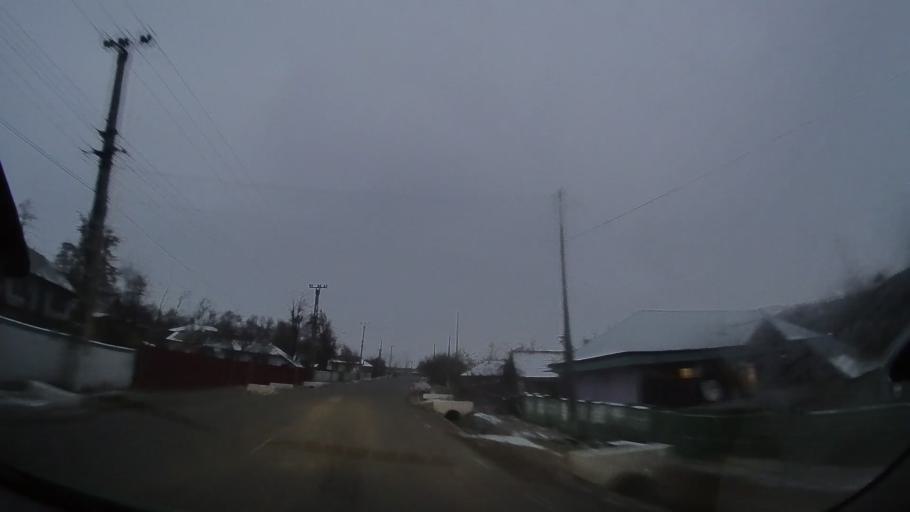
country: RO
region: Vaslui
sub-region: Comuna Vutcani
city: Vutcani
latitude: 46.4145
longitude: 27.9966
